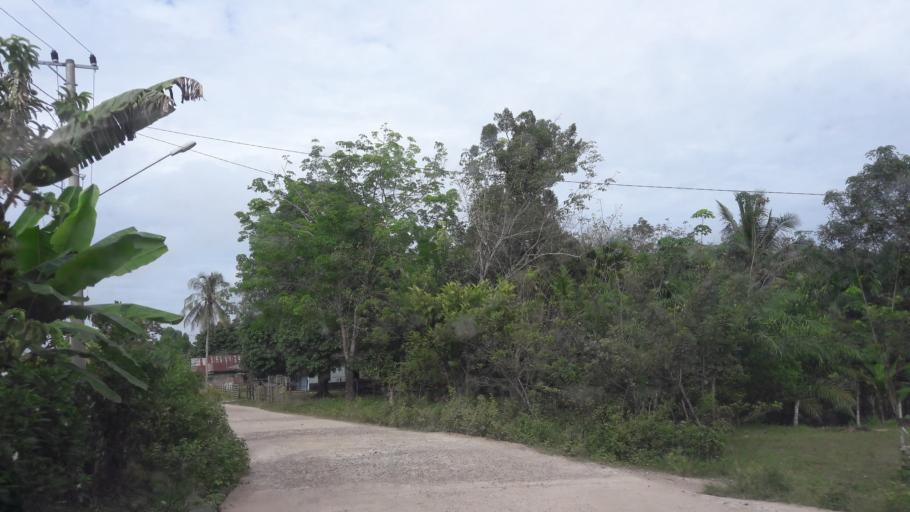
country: ID
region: South Sumatra
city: Gunungmegang Dalam
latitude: -3.2954
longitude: 103.6759
